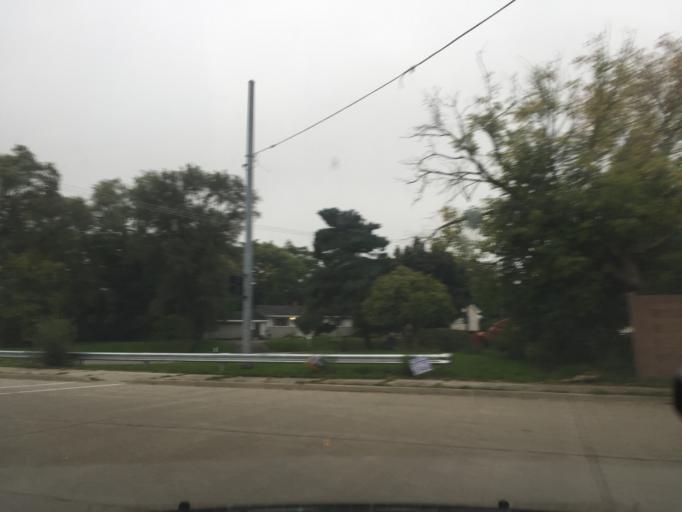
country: US
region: Michigan
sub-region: Oakland County
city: Pontiac
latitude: 42.6257
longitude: -83.2888
